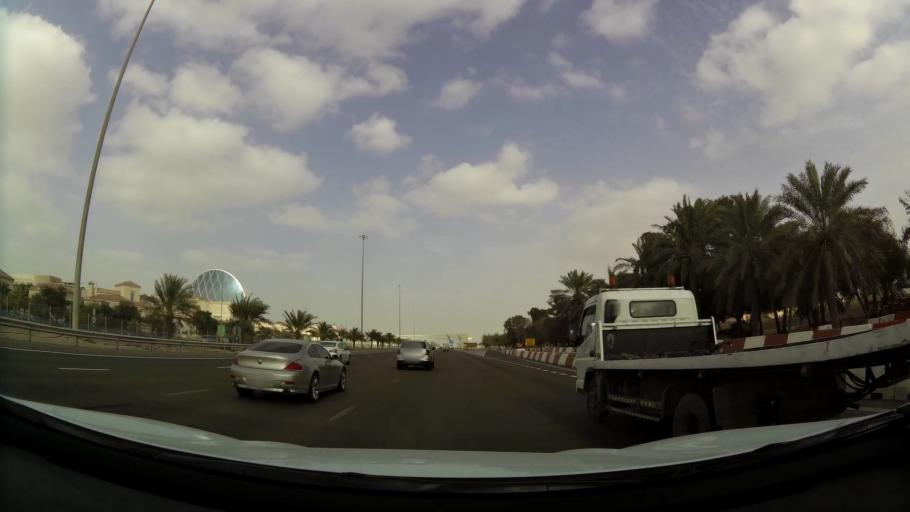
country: AE
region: Abu Dhabi
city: Abu Dhabi
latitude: 24.4366
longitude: 54.5706
